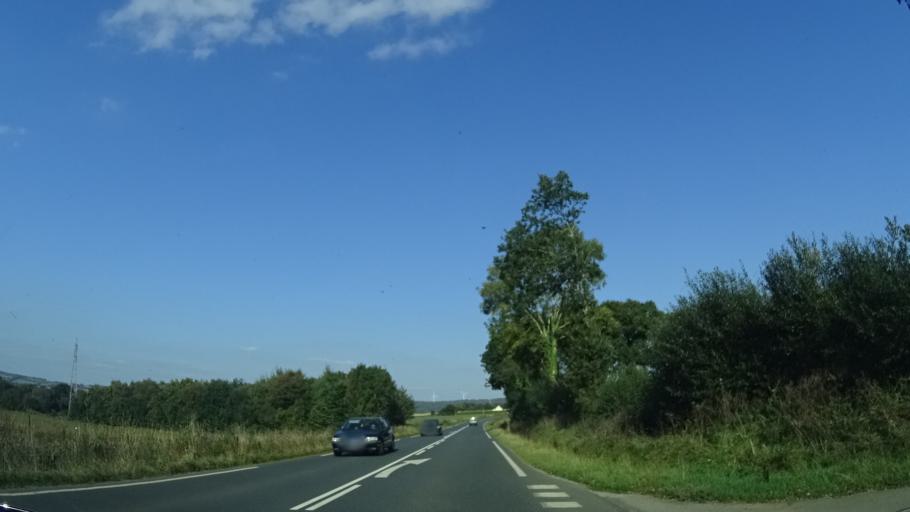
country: FR
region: Brittany
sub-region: Departement du Finistere
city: Cast
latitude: 48.1426
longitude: -4.1614
